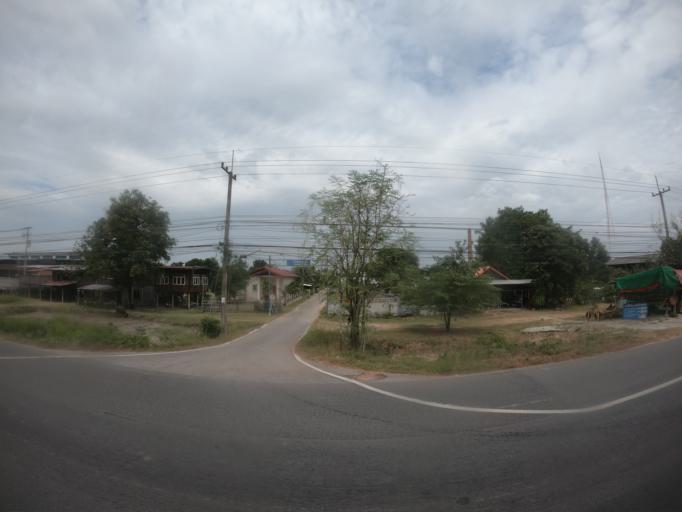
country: TH
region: Roi Et
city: Roi Et
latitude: 16.0741
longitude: 103.5929
